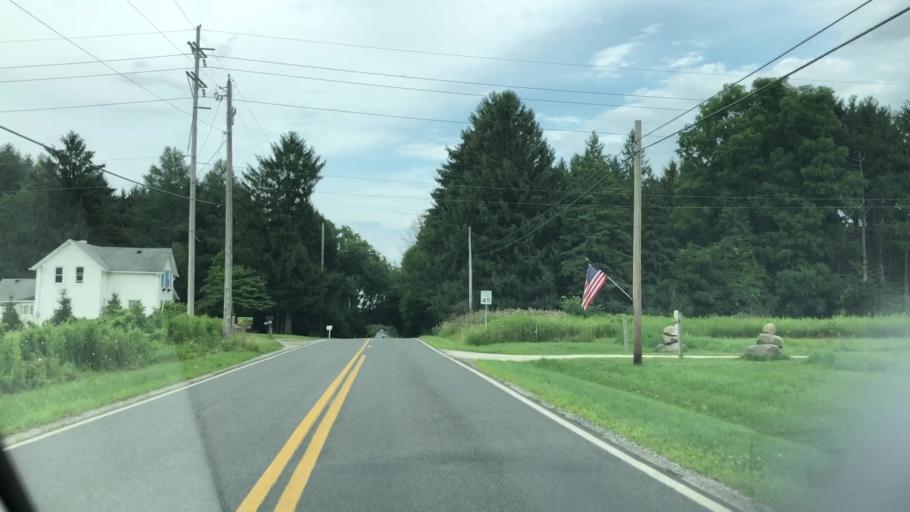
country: US
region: Ohio
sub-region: Summit County
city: Montrose-Ghent
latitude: 41.1178
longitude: -81.6974
